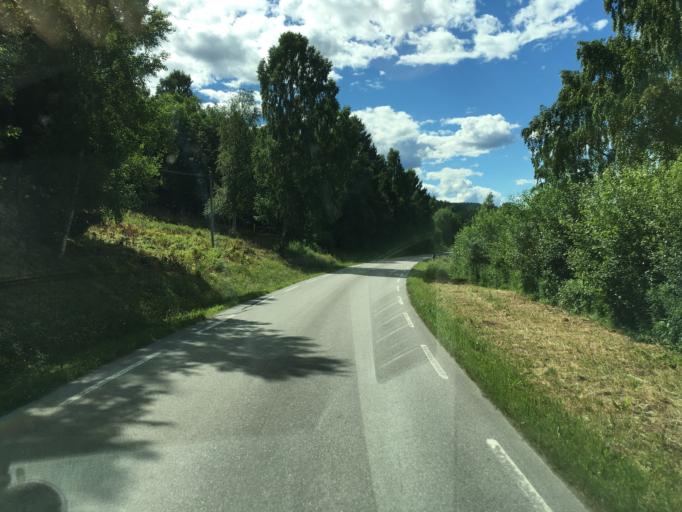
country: NO
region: Oppland
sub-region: Sondre Land
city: Hov
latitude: 60.5115
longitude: 10.3339
